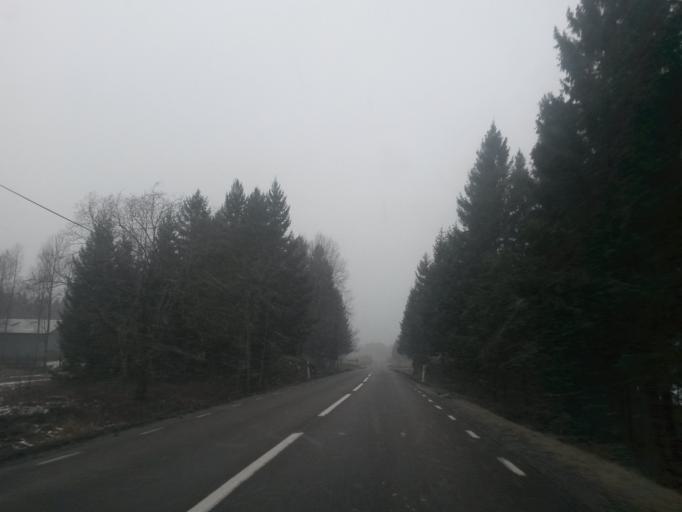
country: SE
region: Vaestra Goetaland
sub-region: Alingsas Kommun
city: Sollebrunn
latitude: 58.2147
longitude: 12.4315
